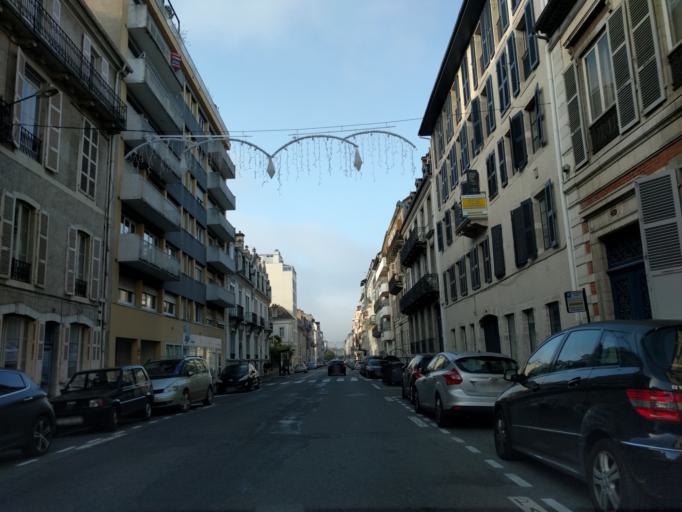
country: FR
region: Aquitaine
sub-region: Departement des Pyrenees-Atlantiques
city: Pau
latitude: 43.3001
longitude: -0.3612
